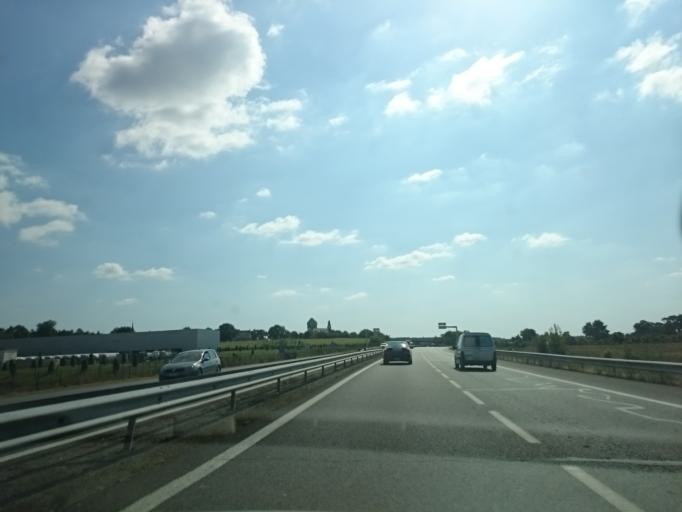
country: FR
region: Brittany
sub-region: Departement d'Ille-et-Vilaine
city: Pance
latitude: 47.8934
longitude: -1.6876
